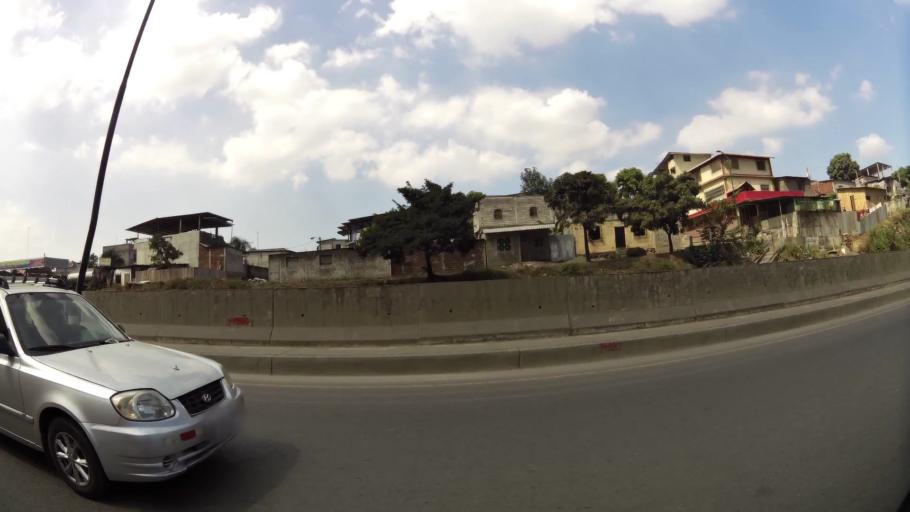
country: EC
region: Guayas
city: Santa Lucia
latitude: -2.1330
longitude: -79.9480
